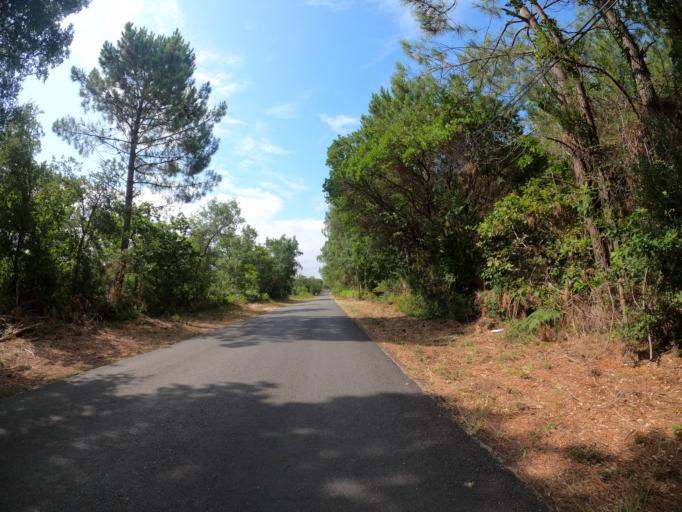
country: FR
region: Aquitaine
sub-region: Departement des Landes
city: Leon
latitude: 43.8931
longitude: -1.3669
